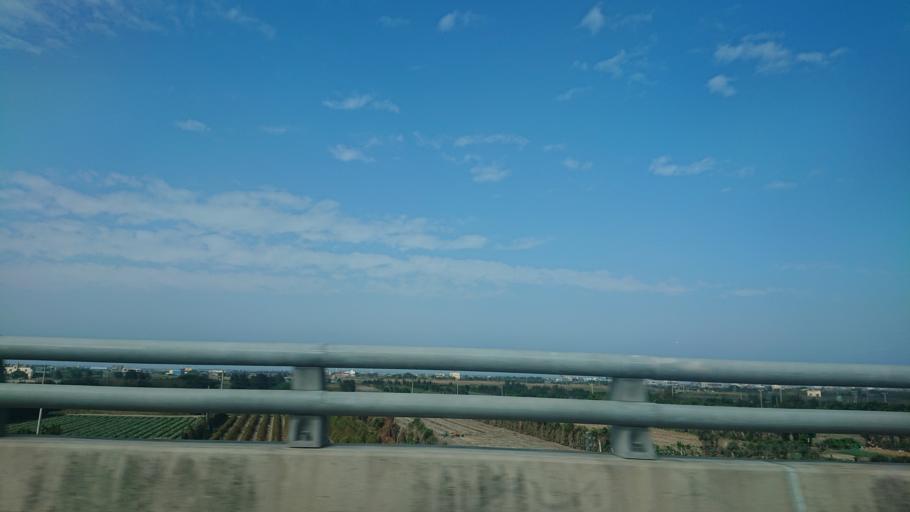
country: TW
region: Taiwan
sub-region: Changhua
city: Chang-hua
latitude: 23.9813
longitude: 120.3649
